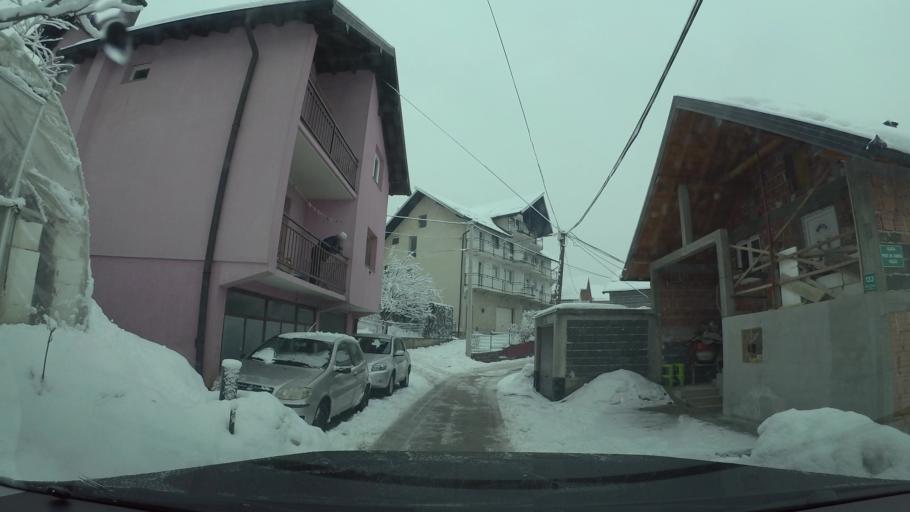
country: BA
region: Federation of Bosnia and Herzegovina
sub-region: Kanton Sarajevo
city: Sarajevo
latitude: 43.8621
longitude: 18.3277
